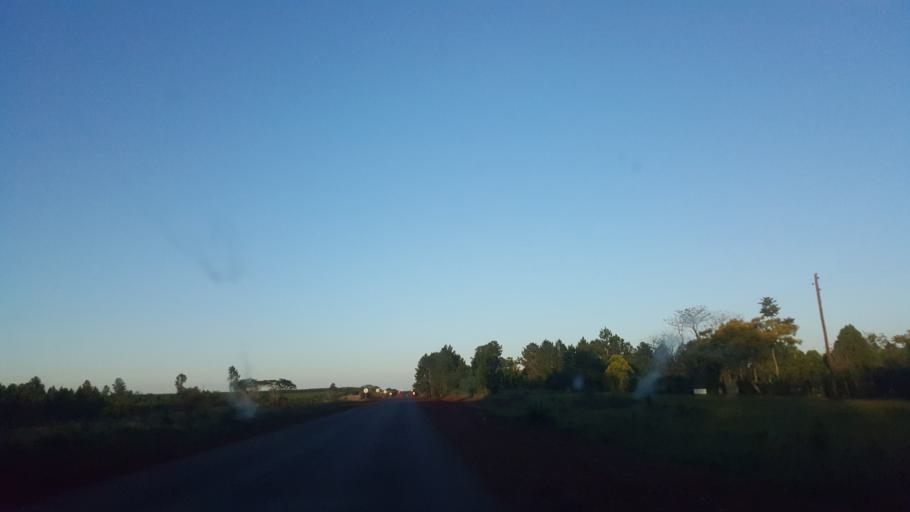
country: AR
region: Corrientes
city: Santo Tome
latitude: -28.5061
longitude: -56.0583
